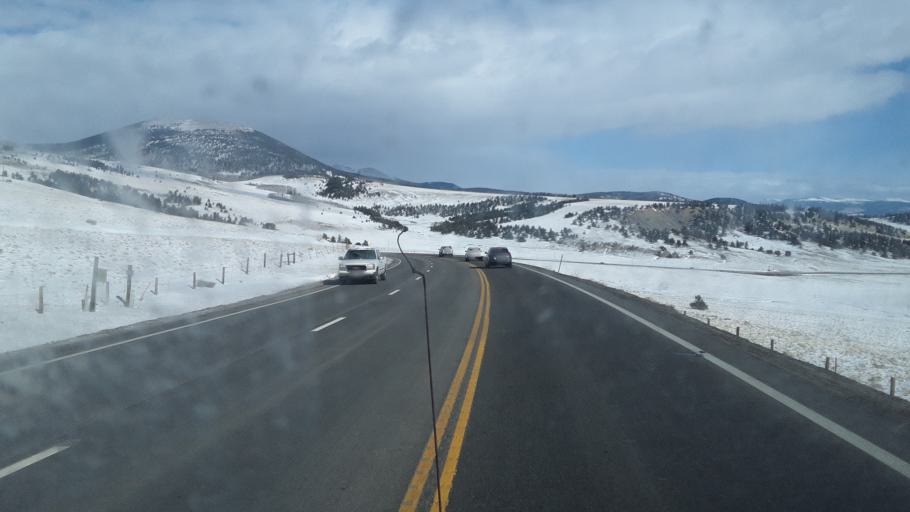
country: US
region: Colorado
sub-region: Park County
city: Fairplay
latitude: 39.2706
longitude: -105.9538
